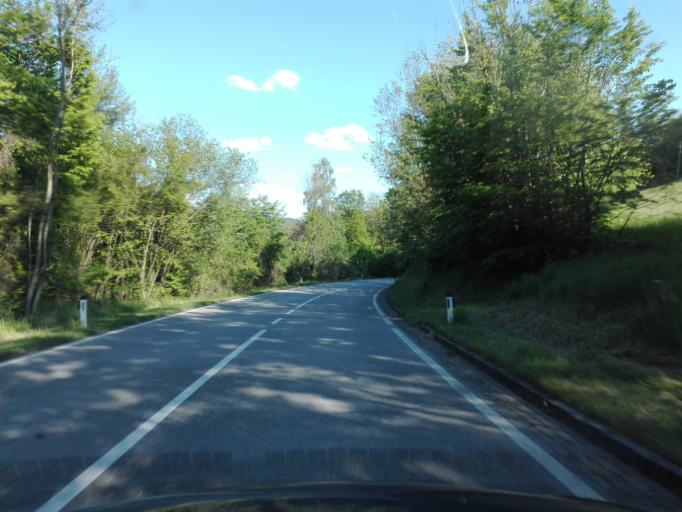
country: AT
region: Upper Austria
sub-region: Politischer Bezirk Rohrbach
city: Pfarrkirchen im Muehlkreis
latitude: 48.4759
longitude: 13.7679
